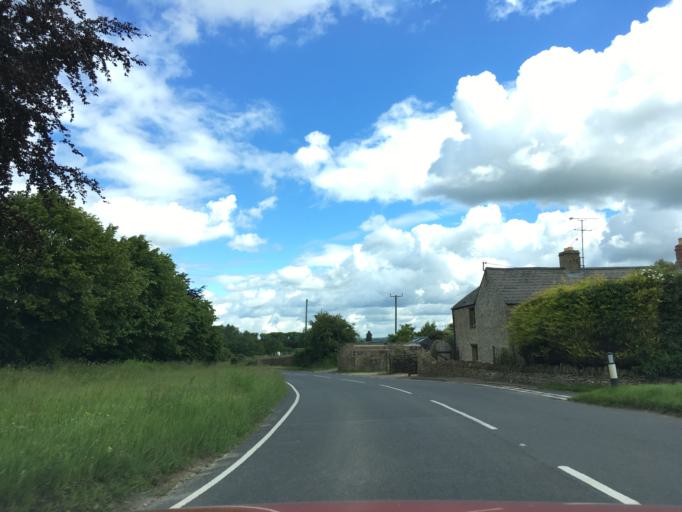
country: GB
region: England
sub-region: Oxfordshire
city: Shipton under Wychwood
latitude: 51.8498
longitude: -1.6010
